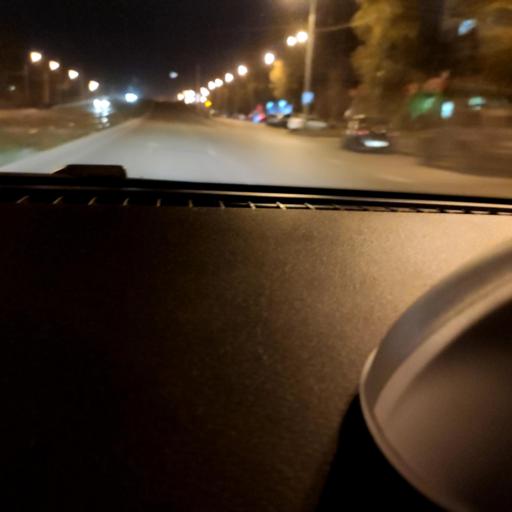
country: RU
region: Samara
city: Smyshlyayevka
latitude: 53.2092
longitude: 50.2811
